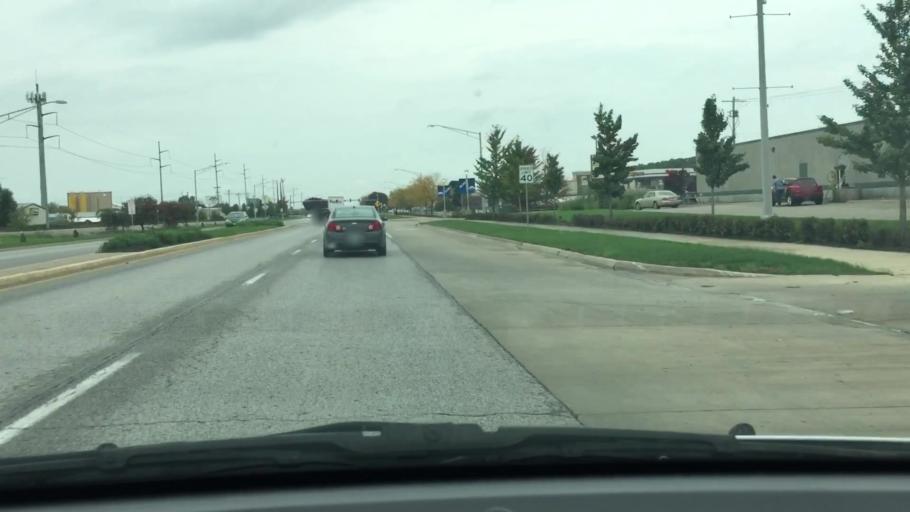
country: US
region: Iowa
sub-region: Johnson County
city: Coralville
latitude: 41.6799
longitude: -91.5921
